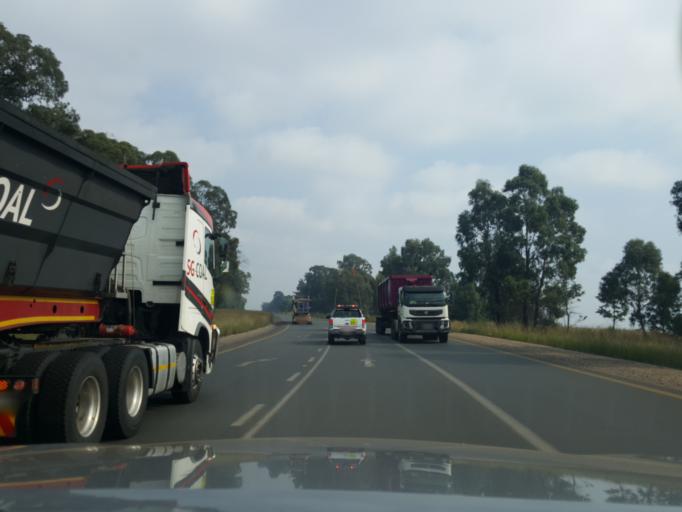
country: ZA
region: Mpumalanga
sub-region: Nkangala District Municipality
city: Witbank
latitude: -25.9905
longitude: 29.2899
